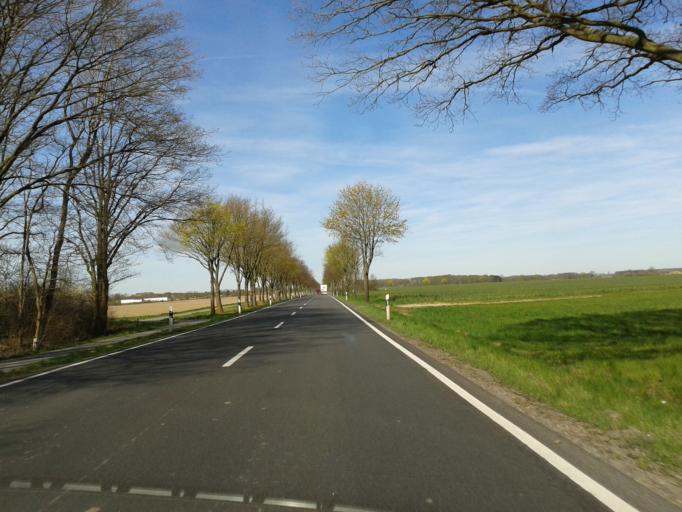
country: DE
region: Lower Saxony
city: Suhlendorf
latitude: 52.9292
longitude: 10.7891
